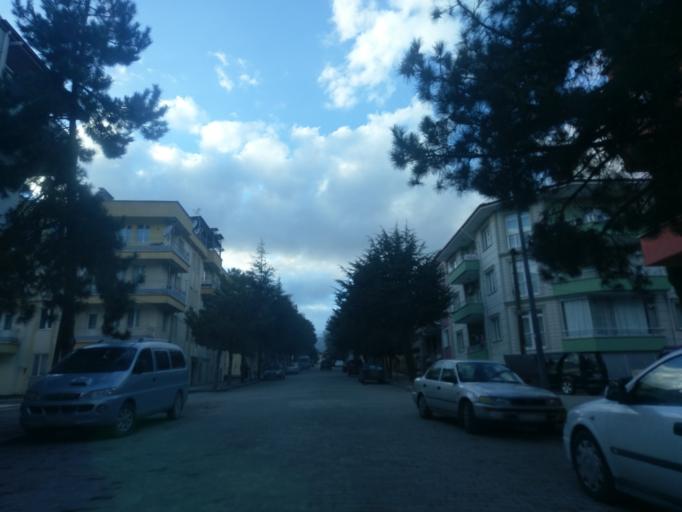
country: TR
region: Kuetahya
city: Gediz
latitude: 38.9900
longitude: 29.3903
